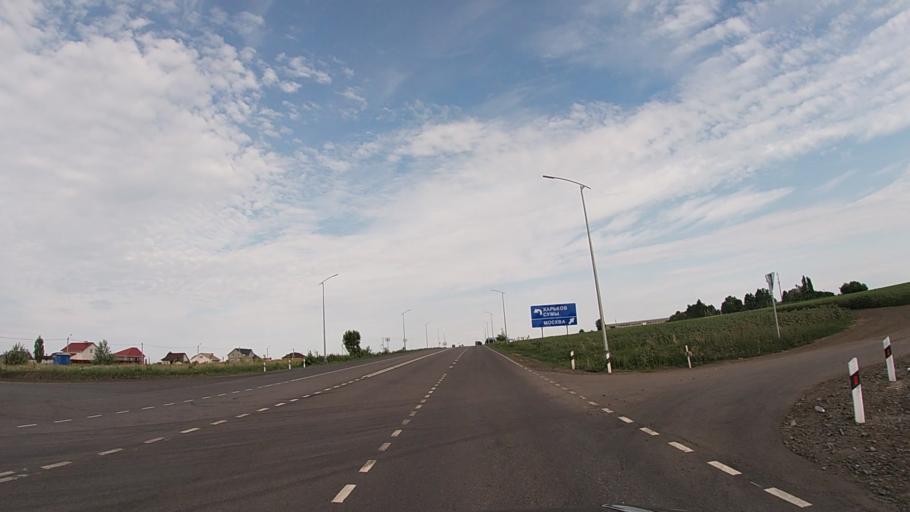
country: RU
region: Belgorod
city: Severnyy
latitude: 50.6718
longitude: 36.4814
